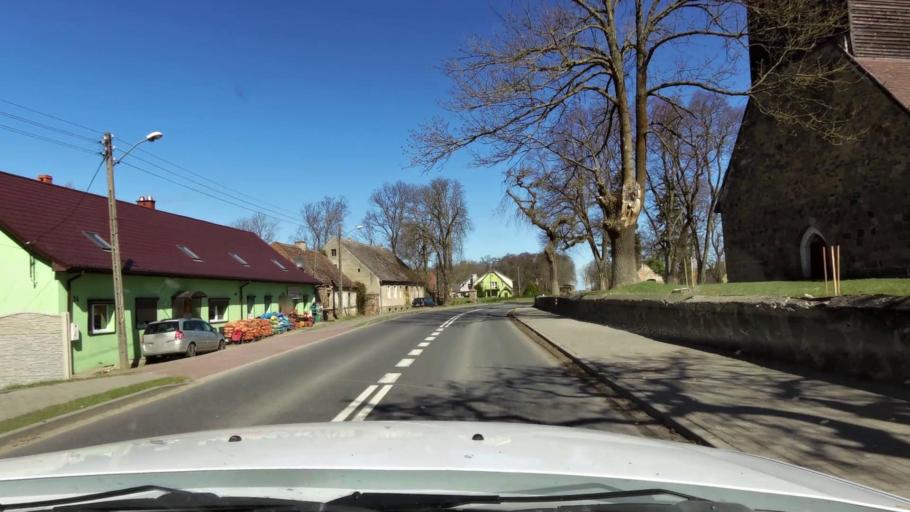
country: PL
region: West Pomeranian Voivodeship
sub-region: Powiat gryfinski
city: Cedynia
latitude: 52.8867
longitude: 14.2866
